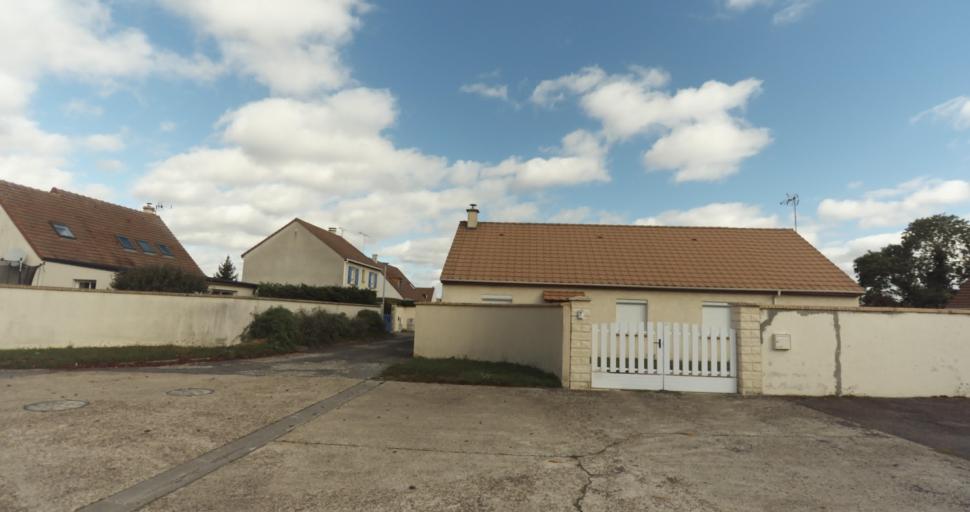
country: FR
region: Centre
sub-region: Departement d'Eure-et-Loir
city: Garnay
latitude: 48.7151
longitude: 1.3379
